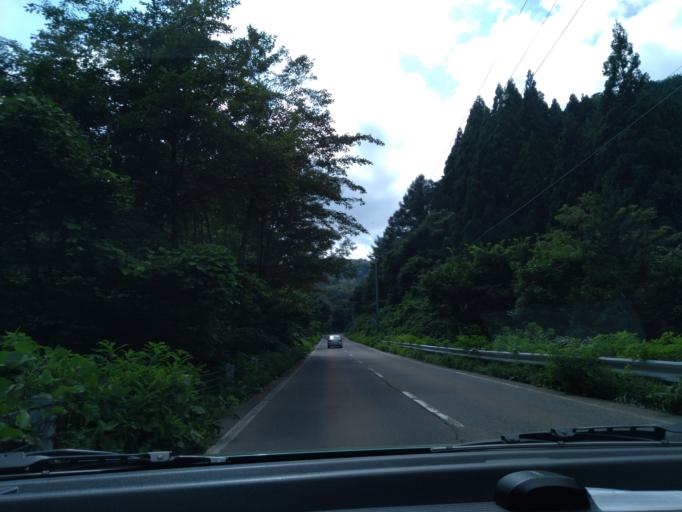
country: JP
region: Iwate
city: Morioka-shi
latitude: 39.6322
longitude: 141.0801
